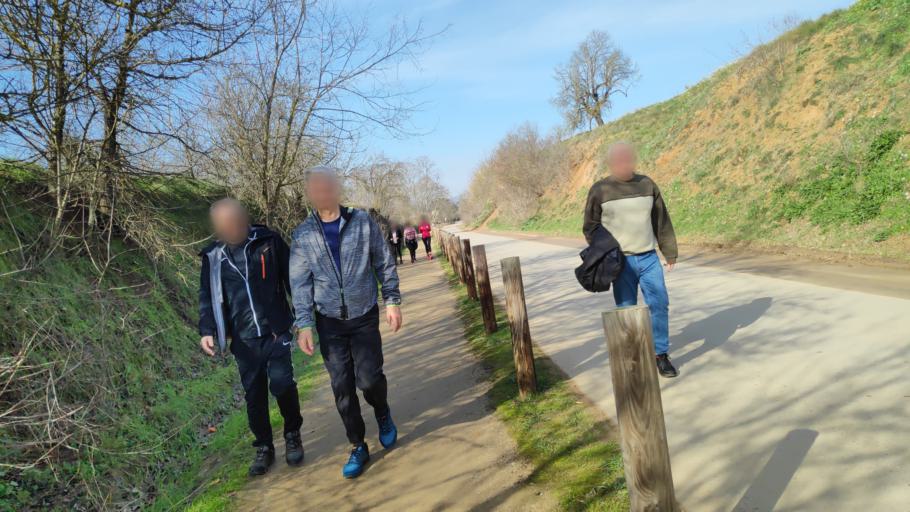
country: ES
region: Catalonia
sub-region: Provincia de Barcelona
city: Mollet del Valles
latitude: 41.5616
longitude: 2.1993
